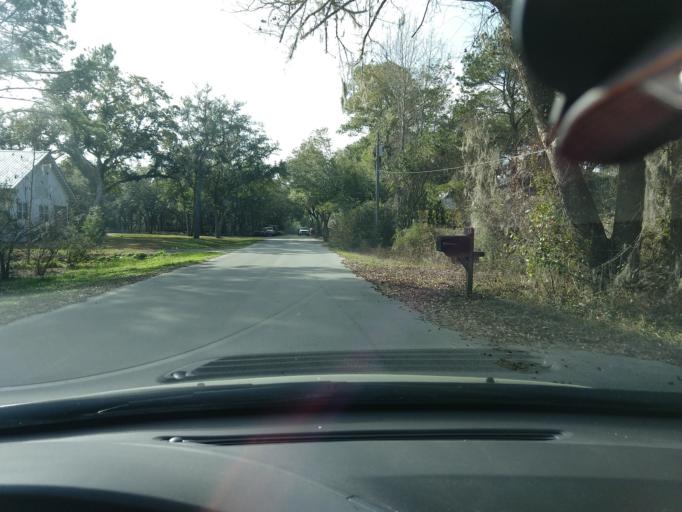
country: US
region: Florida
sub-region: Walton County
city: Seaside
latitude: 30.3787
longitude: -86.1490
